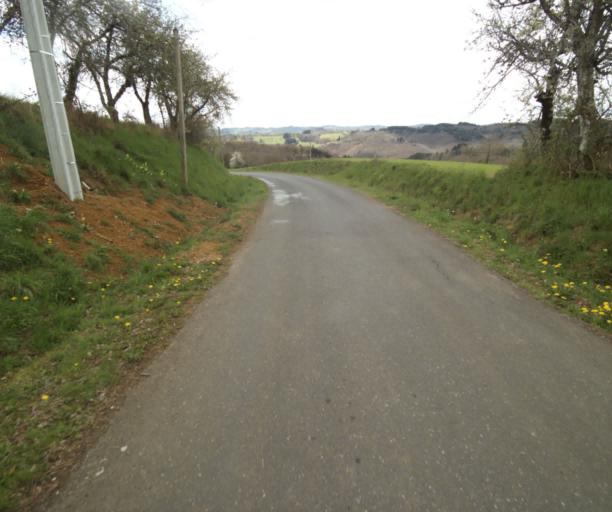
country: FR
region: Limousin
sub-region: Departement de la Correze
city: Sainte-Fortunade
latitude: 45.1967
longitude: 1.8561
